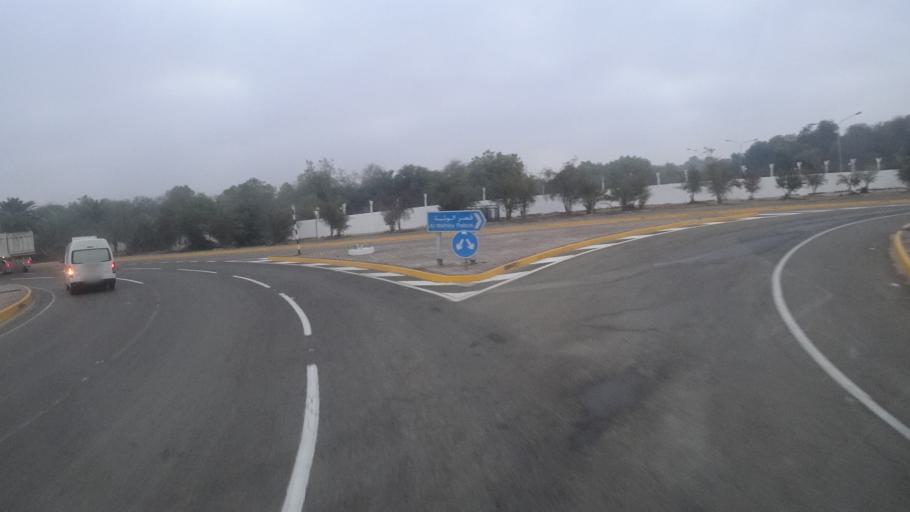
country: AE
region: Abu Dhabi
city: Abu Dhabi
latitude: 24.2294
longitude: 54.6916
